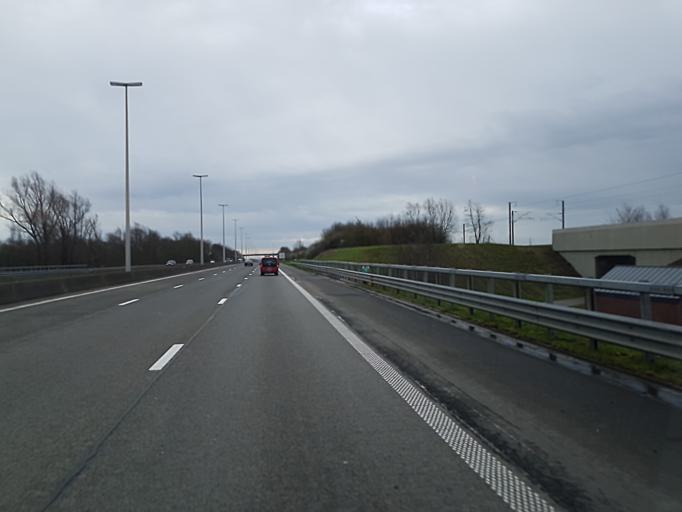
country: BE
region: Flanders
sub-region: Provincie Vlaams-Brabant
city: Tienen
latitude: 50.7618
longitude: 4.9430
